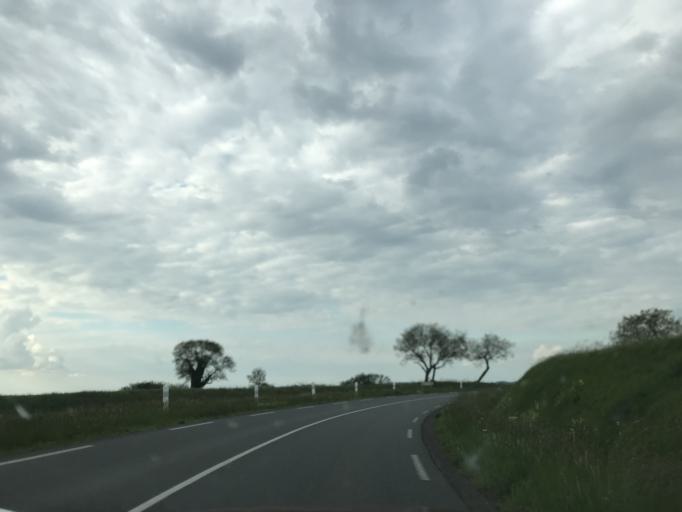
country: FR
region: Auvergne
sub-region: Departement du Puy-de-Dome
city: Maringues
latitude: 45.9552
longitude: 3.3255
